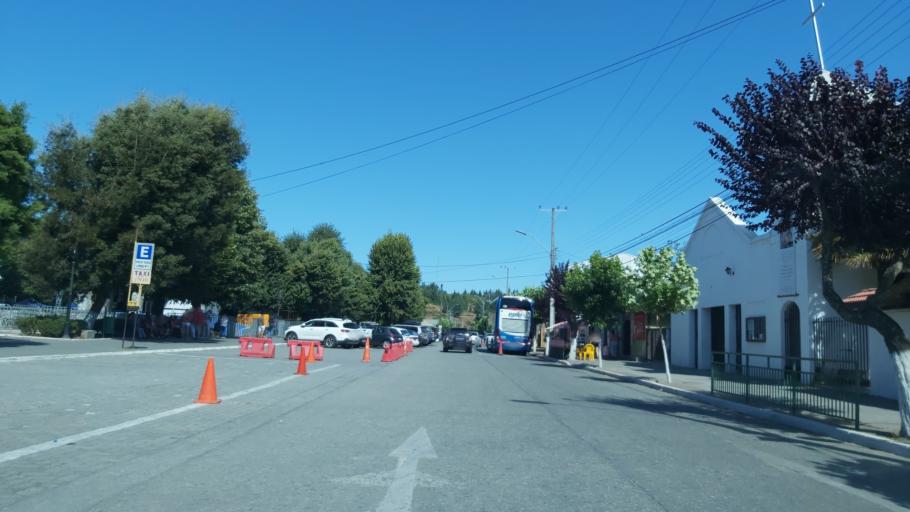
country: CL
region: Biobio
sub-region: Provincia de Concepcion
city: Lota
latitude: -37.1750
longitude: -72.9387
